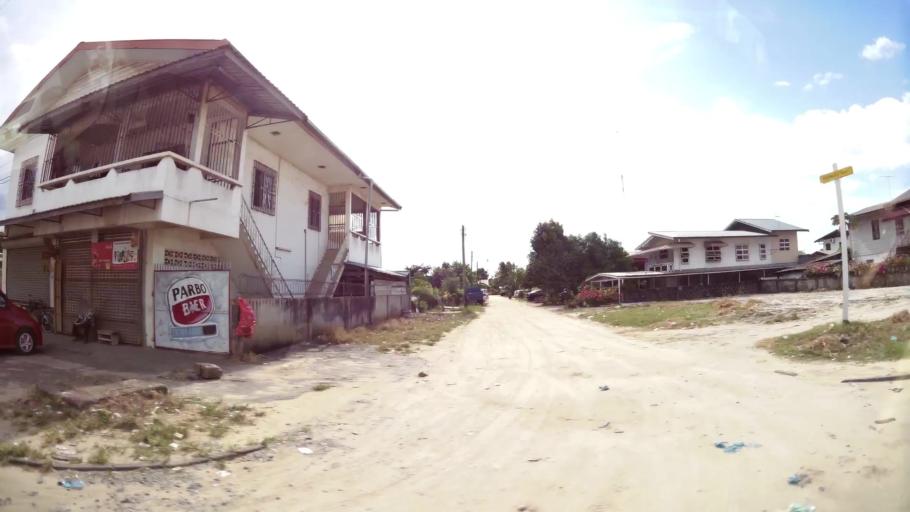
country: SR
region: Paramaribo
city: Paramaribo
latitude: 5.8482
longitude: -55.1541
